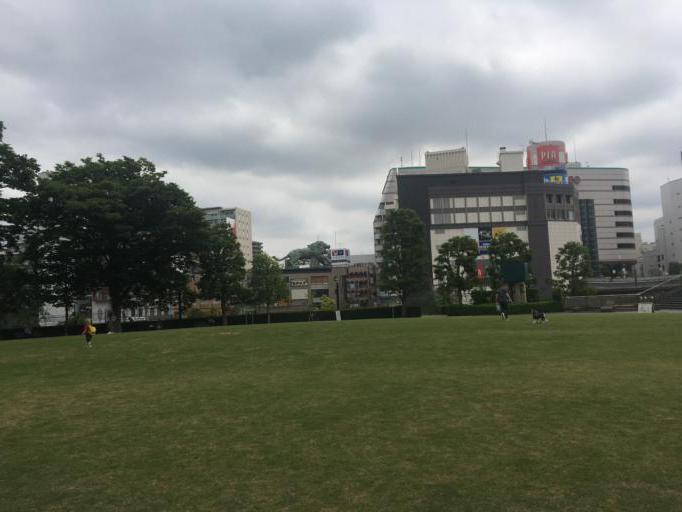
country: JP
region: Saitama
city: Kawaguchi
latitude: 35.8026
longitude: 139.7159
